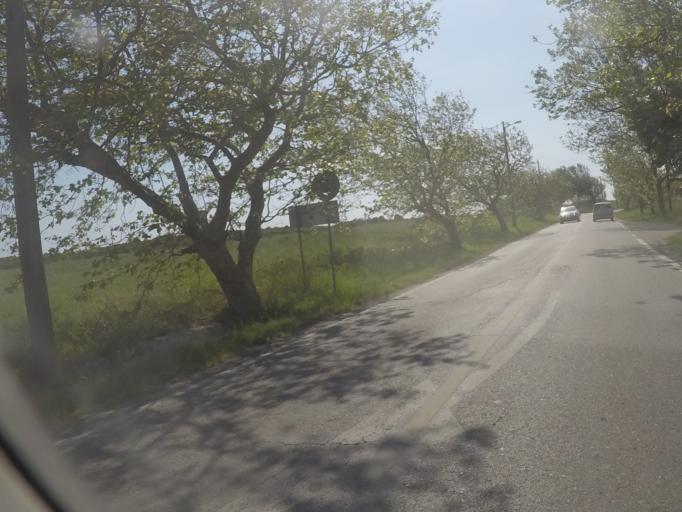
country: PT
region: Setubal
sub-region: Sesimbra
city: Sesimbra
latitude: 38.4427
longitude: -9.1406
